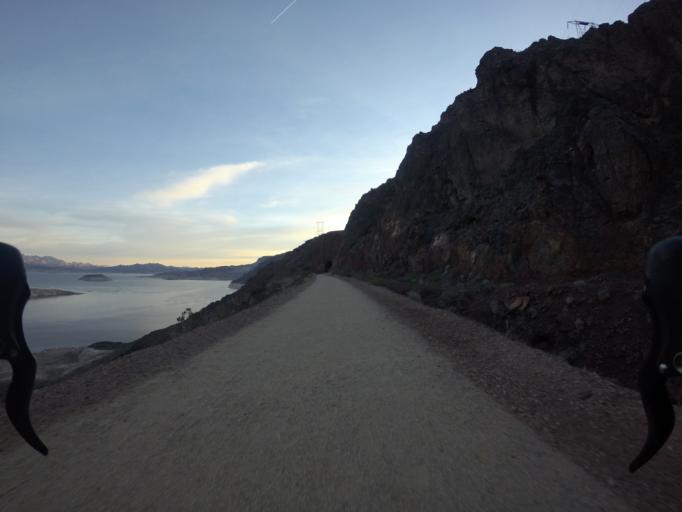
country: US
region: Nevada
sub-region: Clark County
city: Boulder City
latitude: 36.0162
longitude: -114.7643
